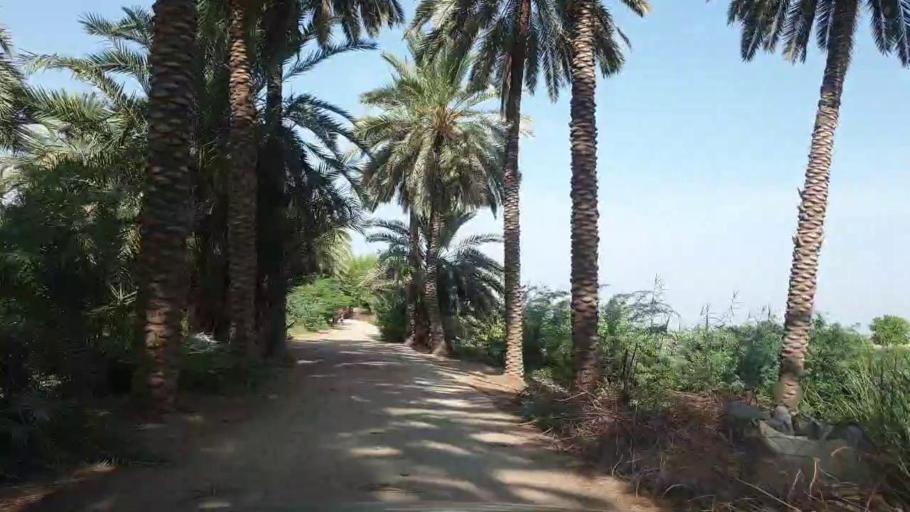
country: PK
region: Sindh
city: Rohri
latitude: 27.6296
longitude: 68.9060
